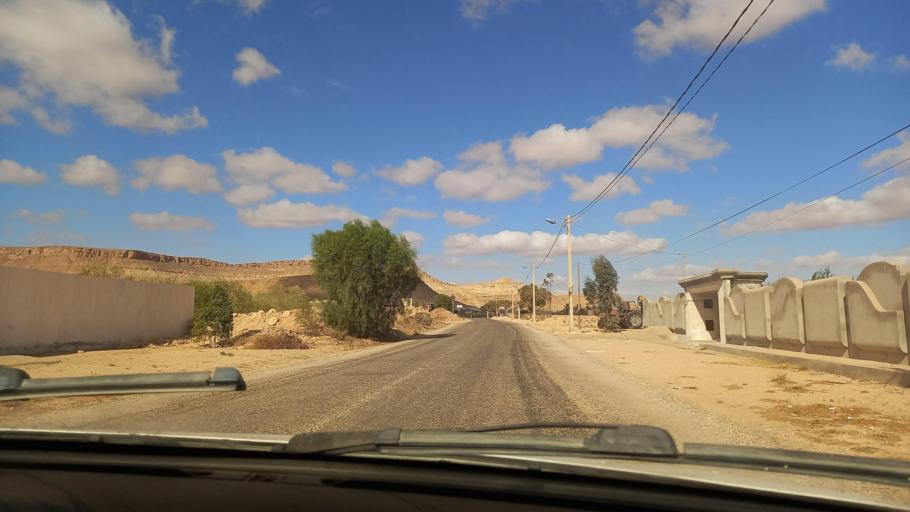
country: TN
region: Tataouine
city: Tataouine
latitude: 32.9784
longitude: 10.2746
